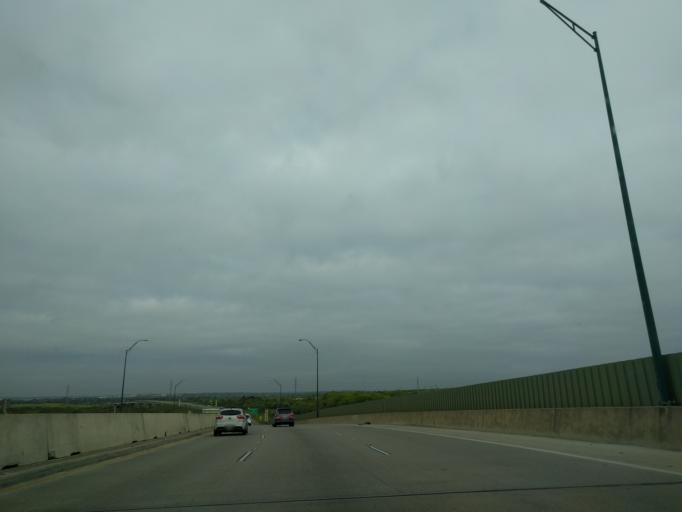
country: US
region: Texas
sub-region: Bexar County
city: Windcrest
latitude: 29.5442
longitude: -98.4273
